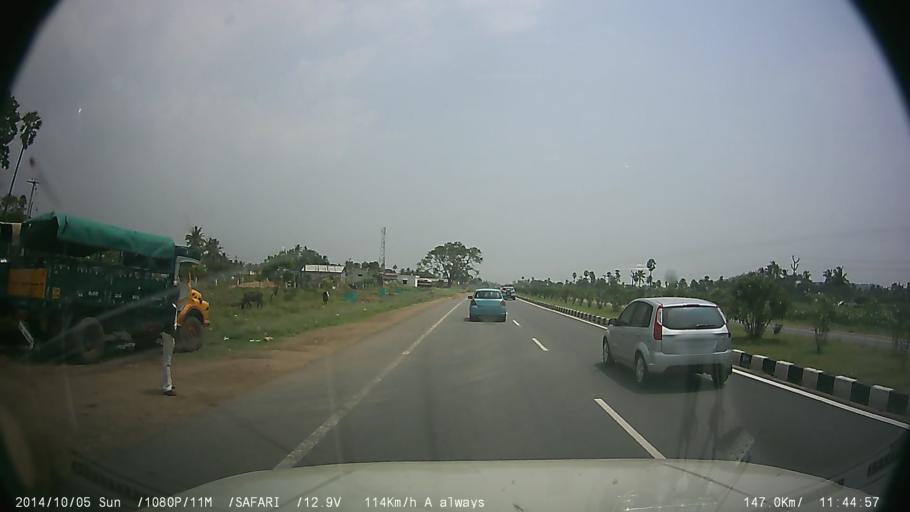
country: IN
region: Tamil Nadu
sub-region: Salem
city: Attur
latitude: 11.5925
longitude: 78.6449
